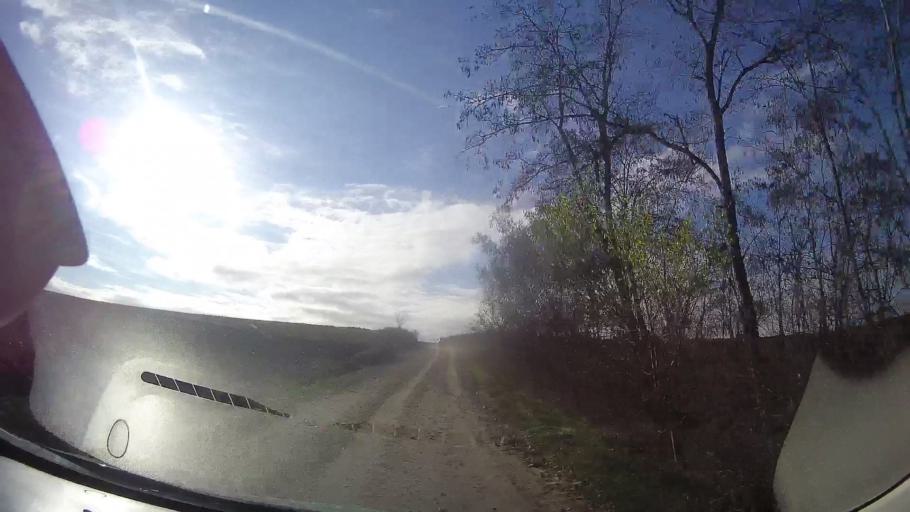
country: RO
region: Mures
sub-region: Comuna Papiu Ilarian
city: Papiu Ilarian
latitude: 46.5729
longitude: 24.2131
